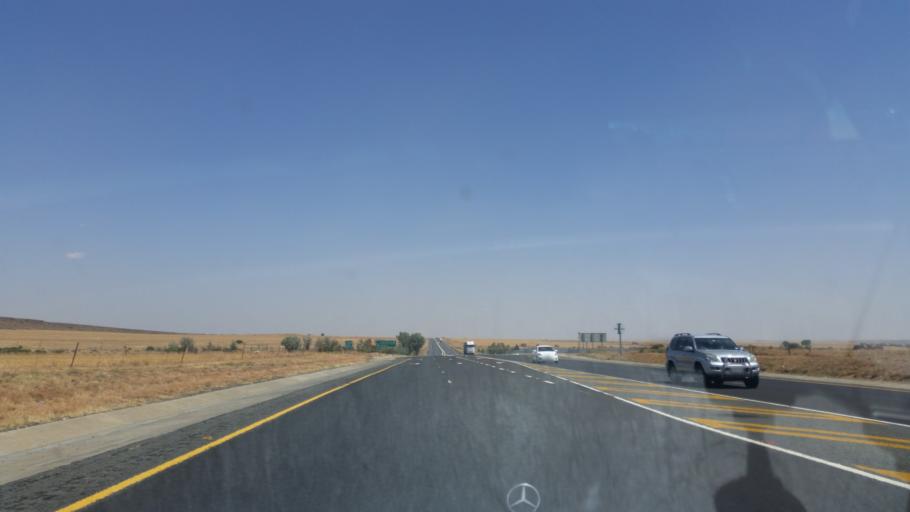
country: ZA
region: Orange Free State
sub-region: Lejweleputswa District Municipality
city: Brandfort
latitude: -28.8150
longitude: 26.6690
